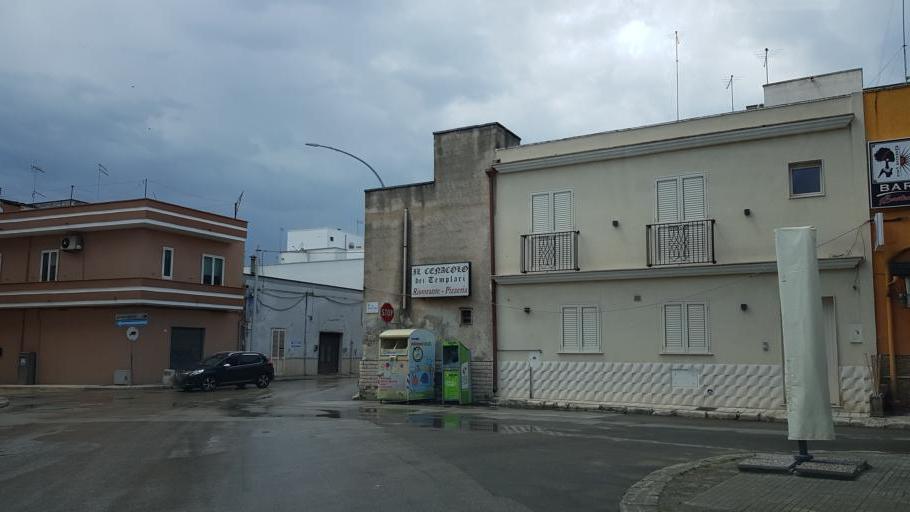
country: IT
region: Apulia
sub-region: Provincia di Brindisi
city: San Donaci
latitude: 40.4466
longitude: 17.9235
